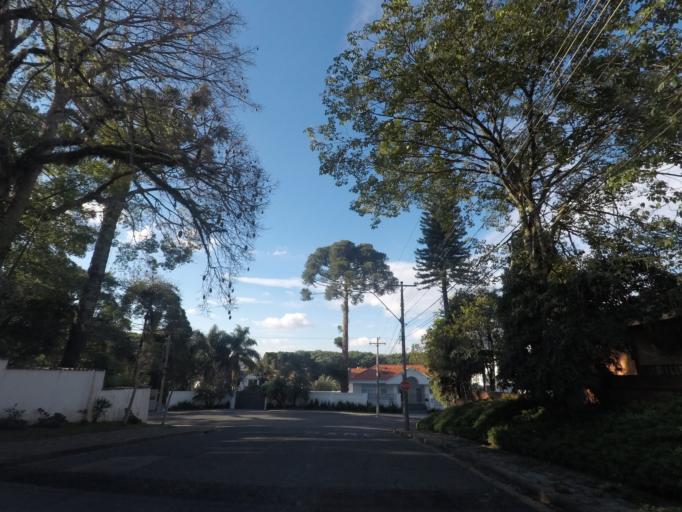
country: BR
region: Parana
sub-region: Curitiba
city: Curitiba
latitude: -25.4522
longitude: -49.3066
